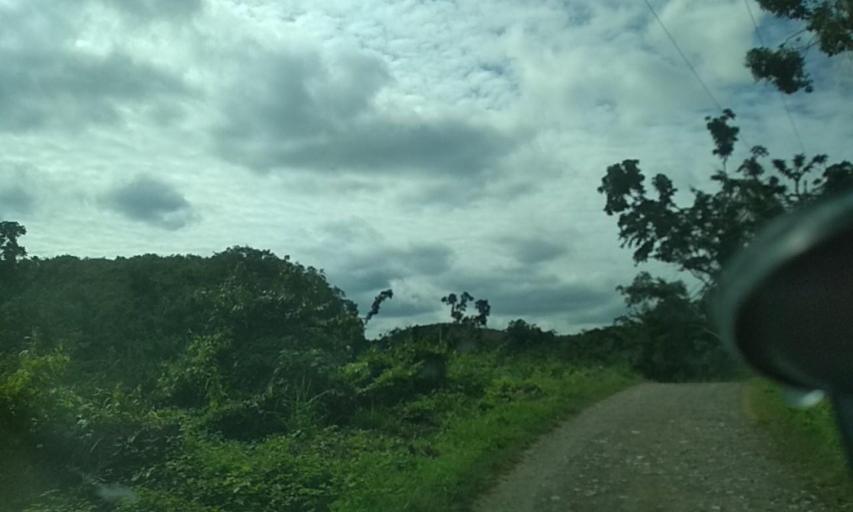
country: MX
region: Veracruz
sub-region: Papantla
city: Polutla
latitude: 20.5658
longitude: -97.1984
